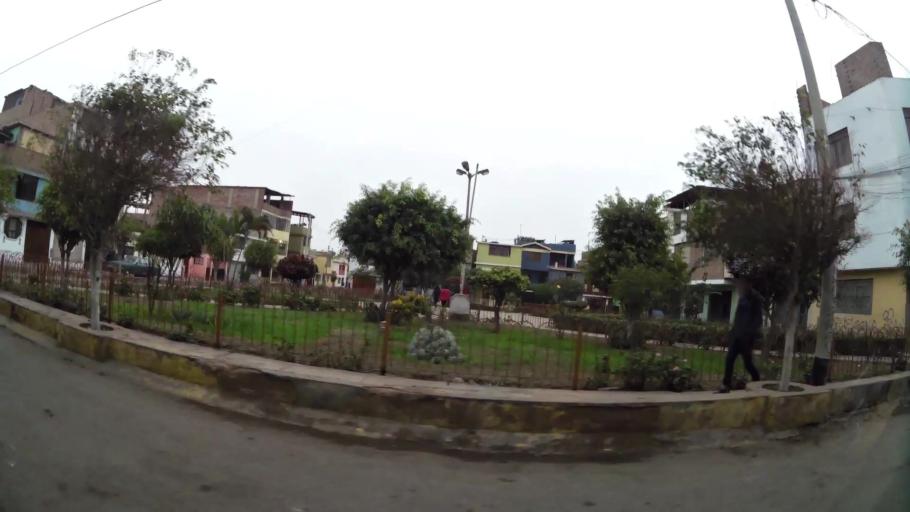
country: PE
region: Lima
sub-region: Lima
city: Surco
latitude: -12.1678
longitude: -76.9746
